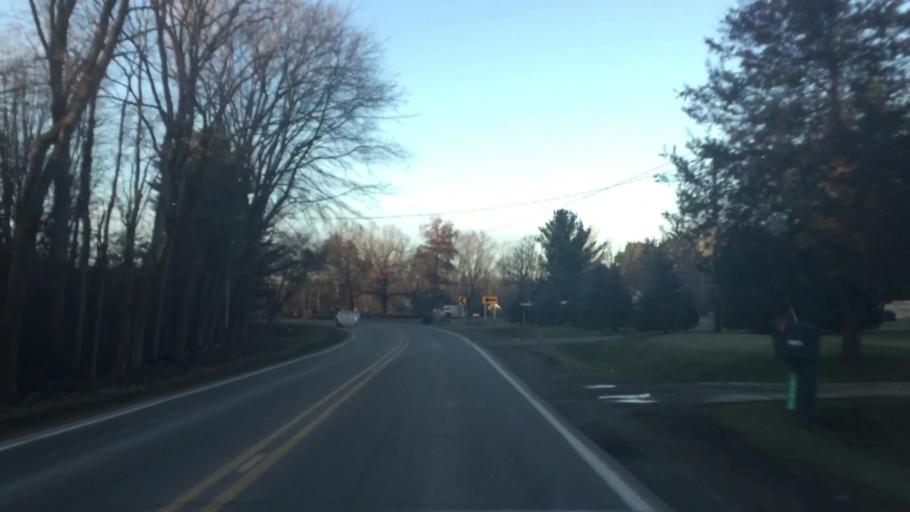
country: US
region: Michigan
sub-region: Genesee County
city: Argentine
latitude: 42.8054
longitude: -83.8380
